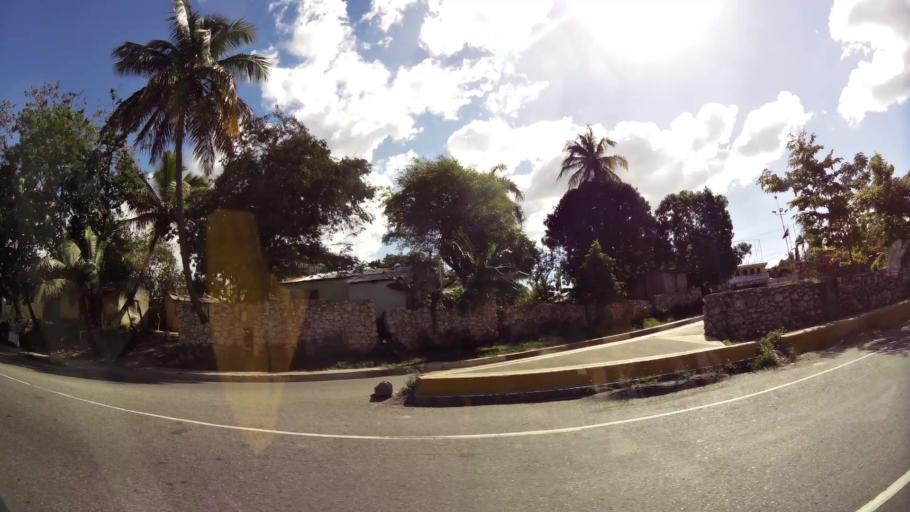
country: DO
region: Santo Domingo
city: Santo Domingo Oeste
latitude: 18.5507
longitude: -70.0532
